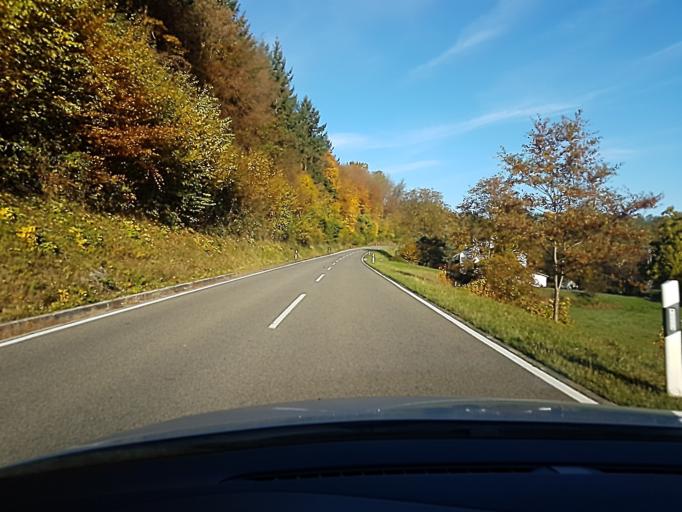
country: DE
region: Baden-Wuerttemberg
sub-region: Karlsruhe Region
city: Billigheim
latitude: 49.3344
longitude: 9.2471
